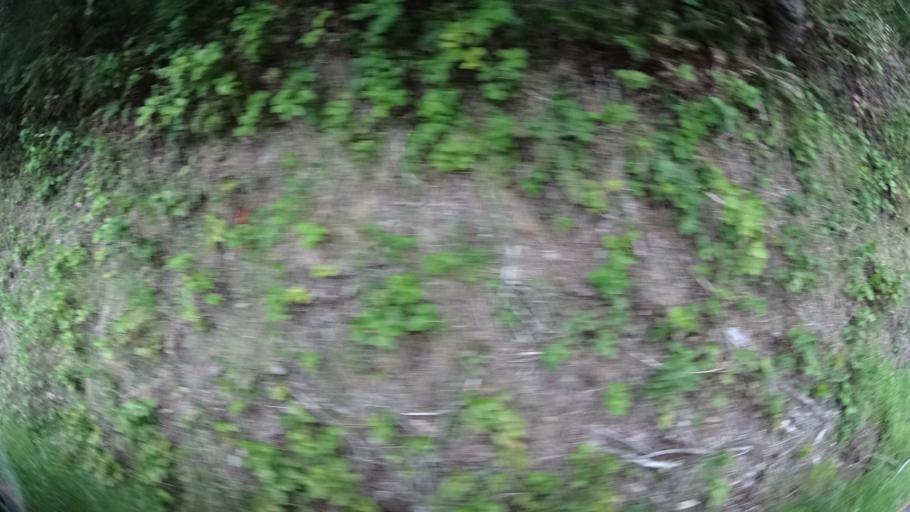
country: US
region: California
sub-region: Humboldt County
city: Ferndale
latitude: 40.5135
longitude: -124.2791
